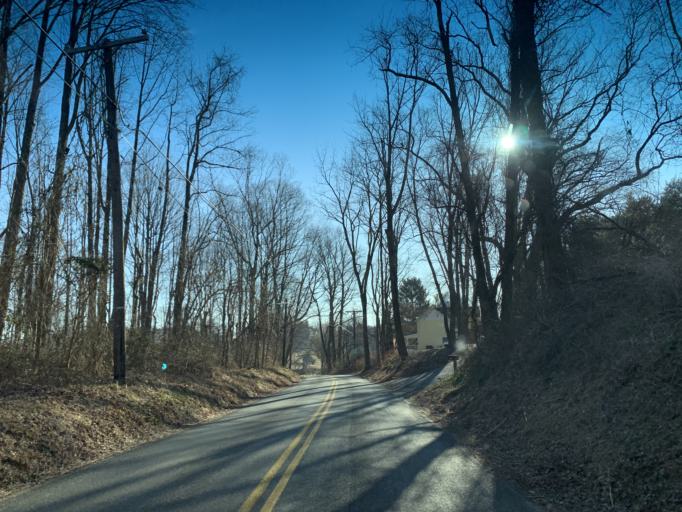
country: US
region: Maryland
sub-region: Harford County
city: Aberdeen
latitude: 39.5887
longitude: -76.2178
